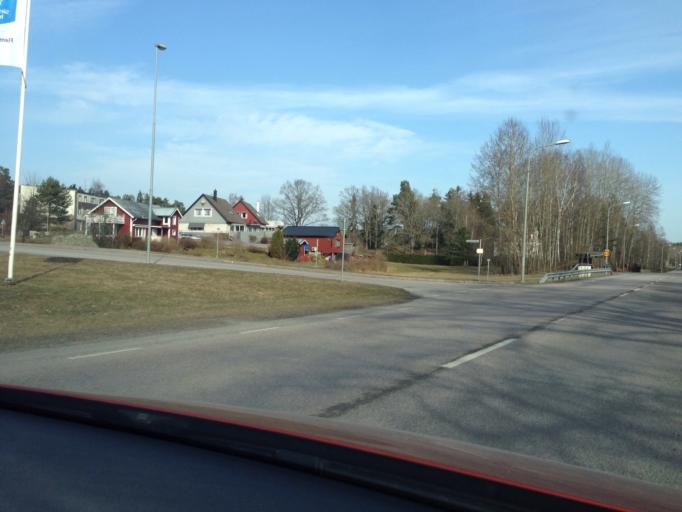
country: SE
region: Soedermanland
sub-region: Flens Kommun
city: Flen
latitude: 59.0546
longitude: 16.6088
